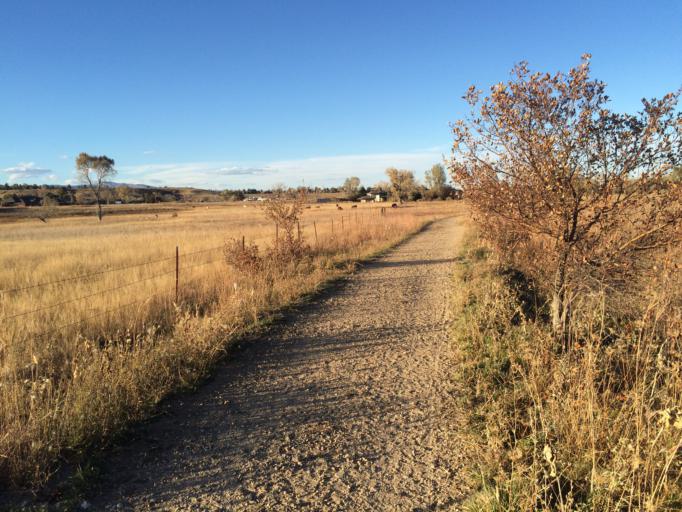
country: US
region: Colorado
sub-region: Boulder County
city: Boulder
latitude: 39.9572
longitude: -105.2396
